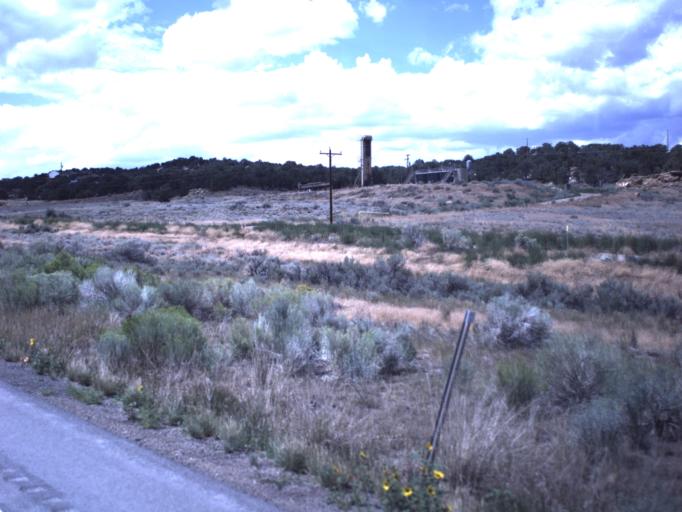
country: US
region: Utah
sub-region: Duchesne County
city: Duchesne
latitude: 40.1714
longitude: -110.5727
